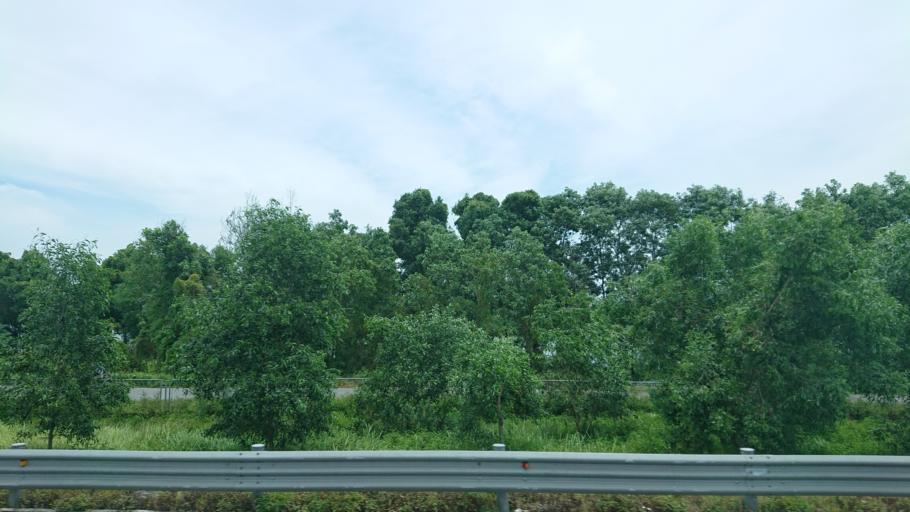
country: VN
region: Hai Phong
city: Tien Lang
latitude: 20.7709
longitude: 106.5936
